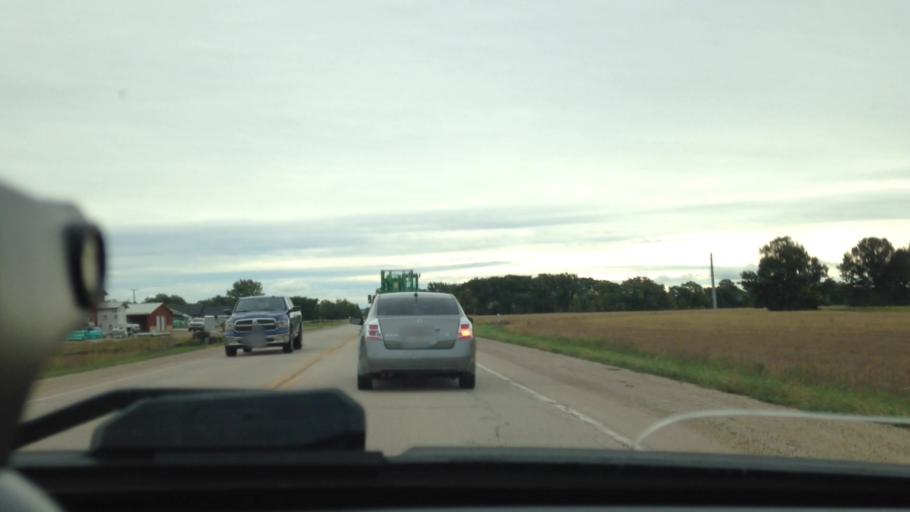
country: US
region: Wisconsin
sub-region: Fond du Lac County
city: North Fond du Lac
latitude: 43.8034
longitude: -88.4996
